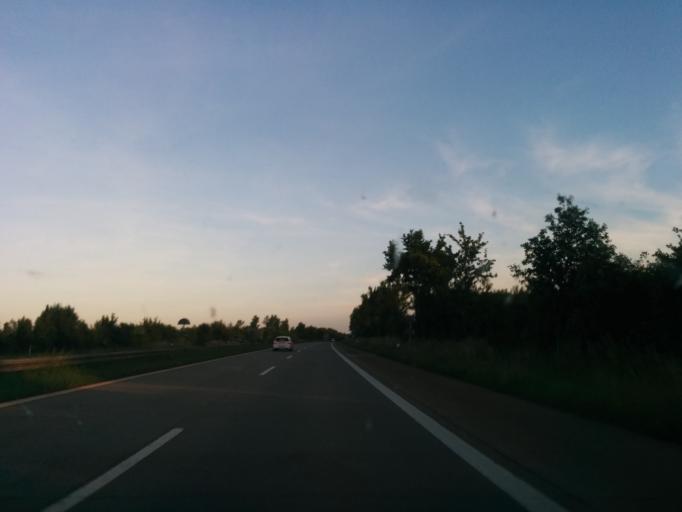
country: DE
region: Bavaria
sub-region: Regierungsbezirk Mittelfranken
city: Uffenheim
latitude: 49.5183
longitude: 10.1959
